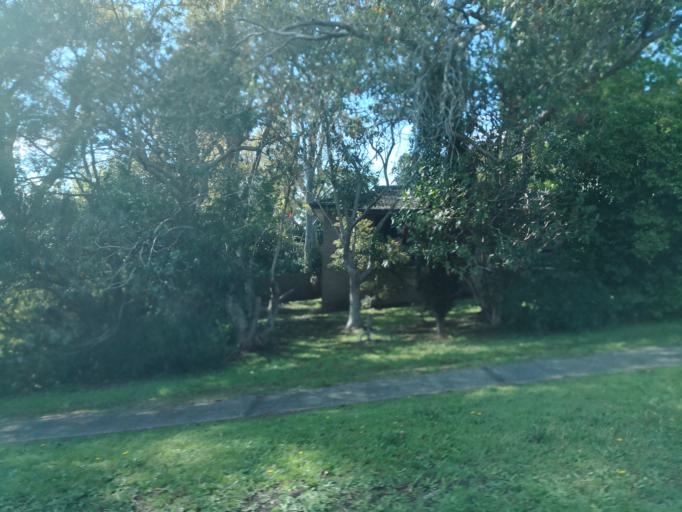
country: AU
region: New South Wales
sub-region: Gosford Shire
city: Gosford
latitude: -33.4130
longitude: 151.3449
